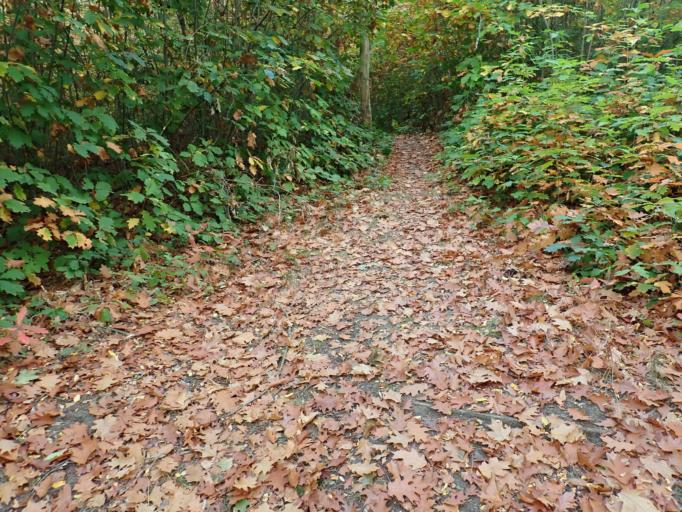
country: BE
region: Flanders
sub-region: Provincie Antwerpen
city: Herenthout
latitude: 51.1299
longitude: 4.7134
